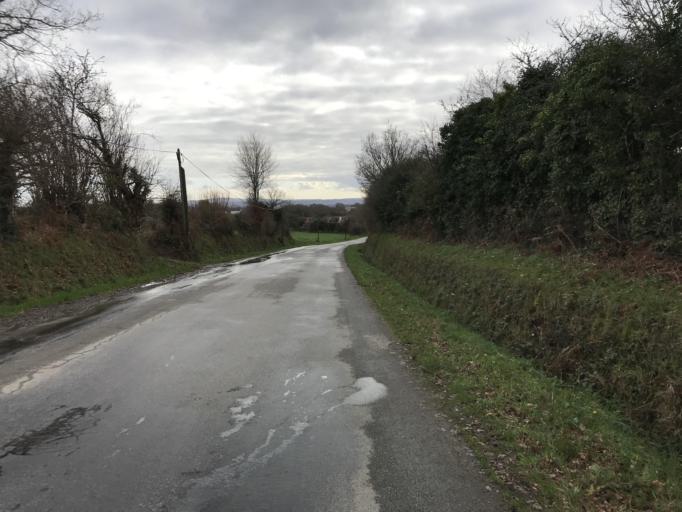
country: FR
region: Brittany
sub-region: Departement du Finistere
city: Plougastel-Daoulas
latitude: 48.3756
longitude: -4.3506
